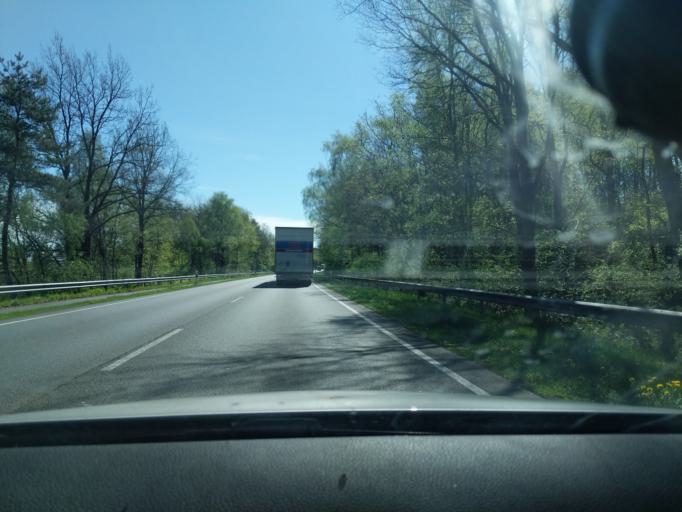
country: DE
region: Lower Saxony
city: Buxtehude
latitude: 53.4609
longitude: 9.7146
